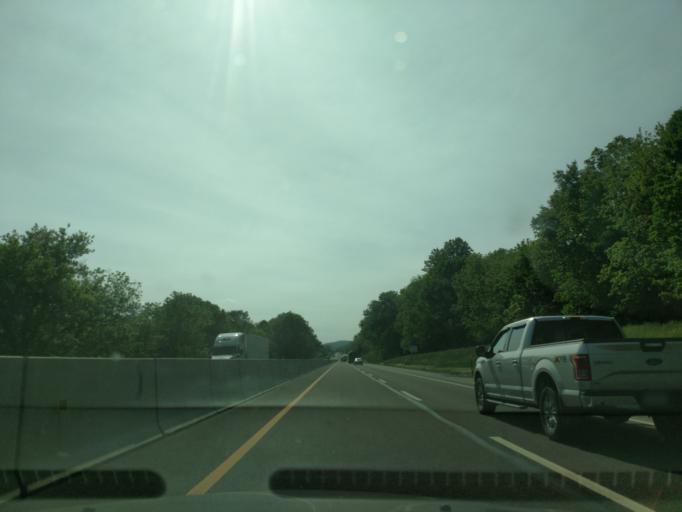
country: US
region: Pennsylvania
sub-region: Lancaster County
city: Schoeneck
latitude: 40.2454
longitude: -76.1837
